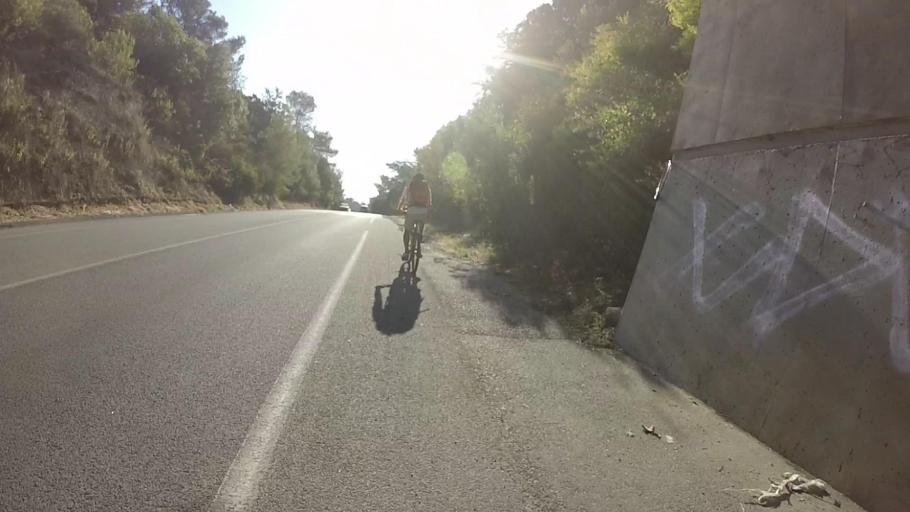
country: FR
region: Provence-Alpes-Cote d'Azur
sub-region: Departement des Alpes-Maritimes
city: Mougins
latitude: 43.6120
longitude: 7.0245
